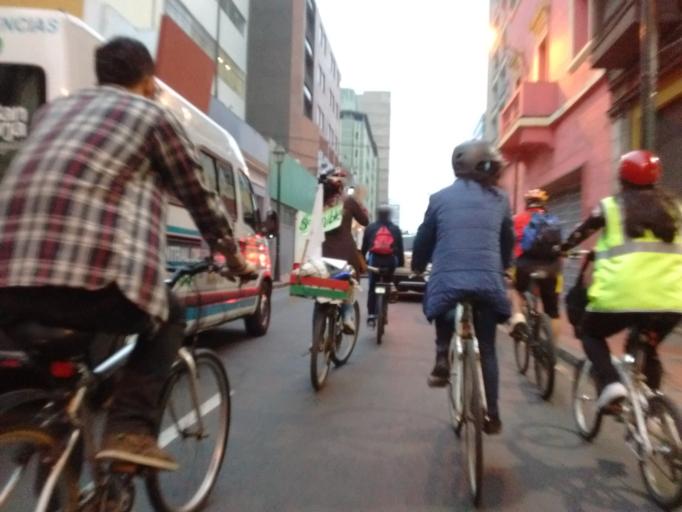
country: PE
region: Lima
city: Lima
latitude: -12.0476
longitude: -77.0339
